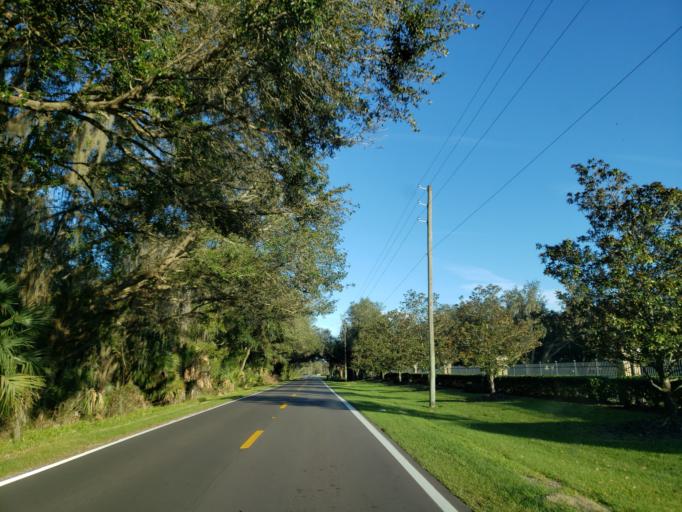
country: US
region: Florida
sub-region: Hillsborough County
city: Boyette
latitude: 27.8214
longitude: -82.2104
